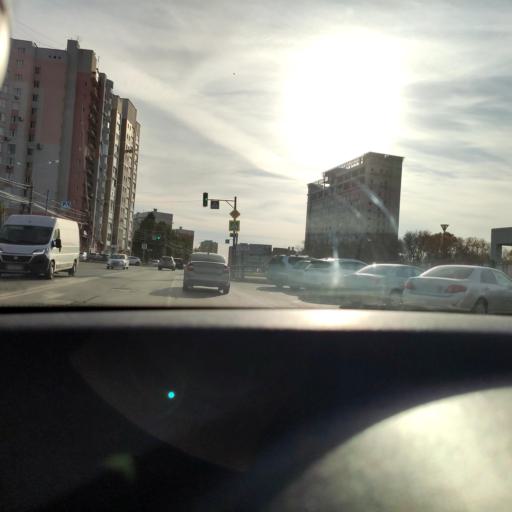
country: RU
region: Samara
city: Samara
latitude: 53.2613
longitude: 50.2084
